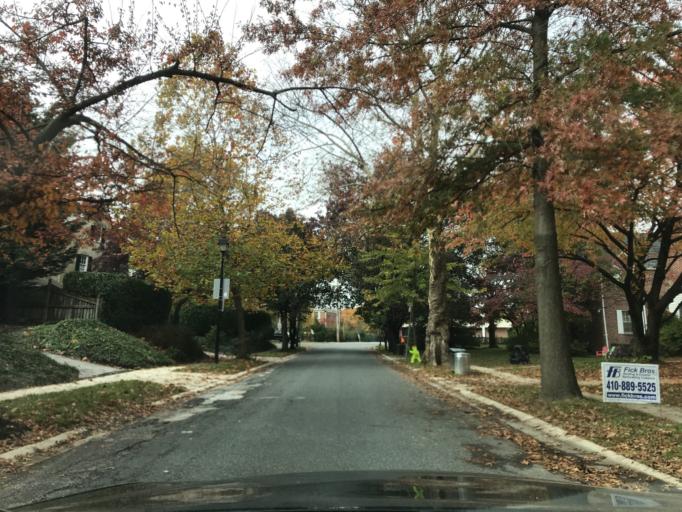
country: US
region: Maryland
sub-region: Baltimore County
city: Towson
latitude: 39.3828
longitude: -76.6063
